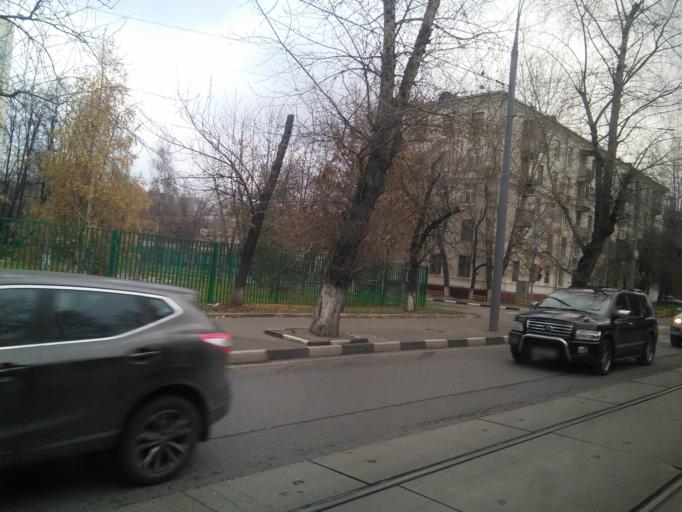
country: RU
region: Moscow
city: Lefortovo
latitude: 55.7632
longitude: 37.7075
